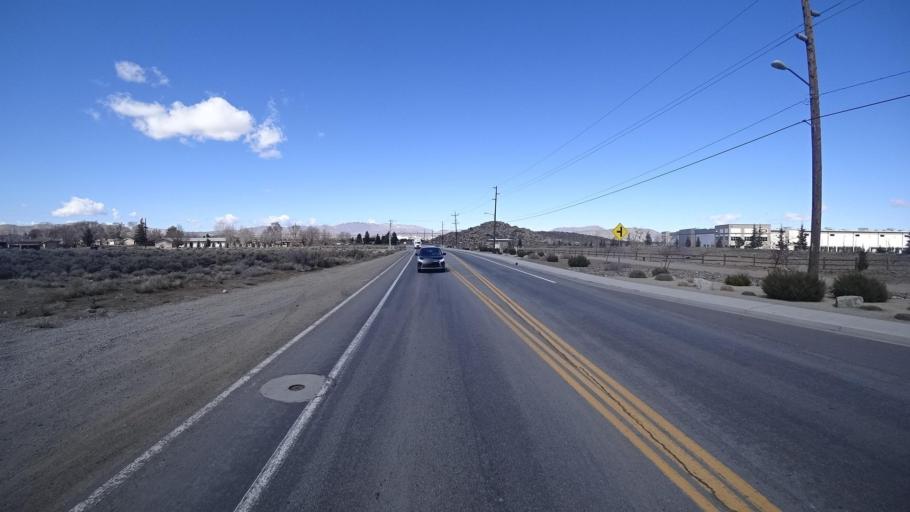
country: US
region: Nevada
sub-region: Washoe County
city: Lemmon Valley
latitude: 39.6307
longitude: -119.8530
